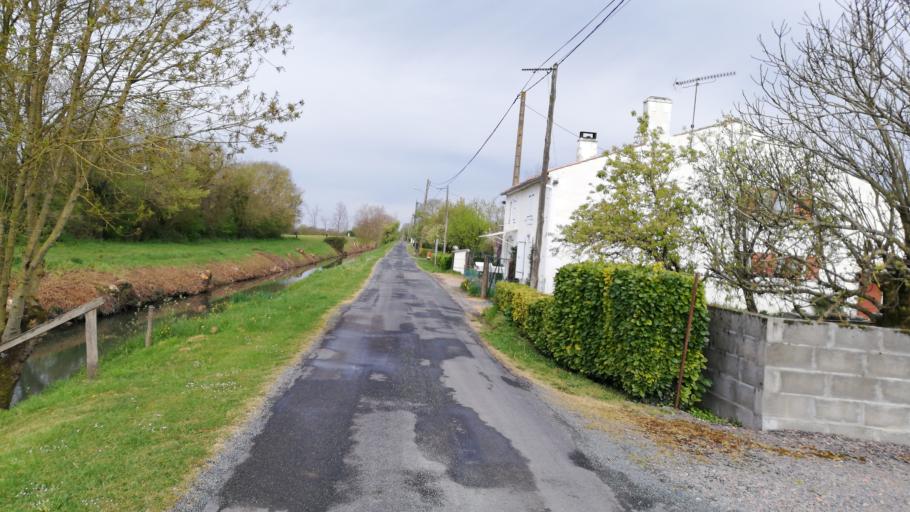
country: FR
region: Pays de la Loire
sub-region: Departement de la Vendee
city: Maillezais
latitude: 46.3283
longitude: -0.7169
